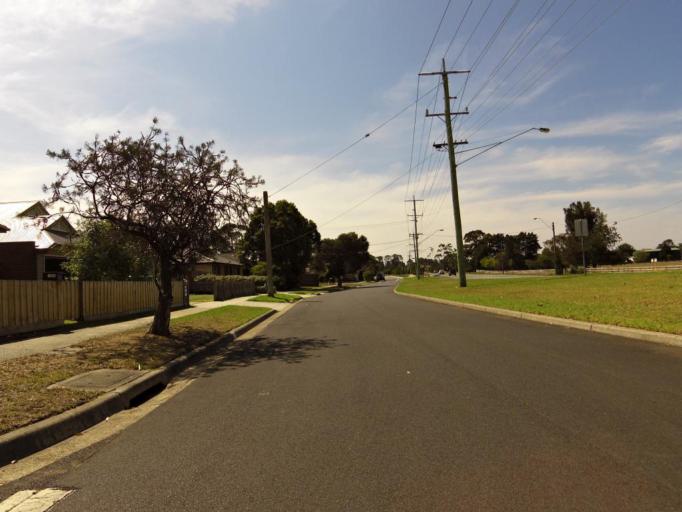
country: AU
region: Victoria
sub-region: Mornington Peninsula
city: Tyabb
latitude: -38.2562
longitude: 145.1895
